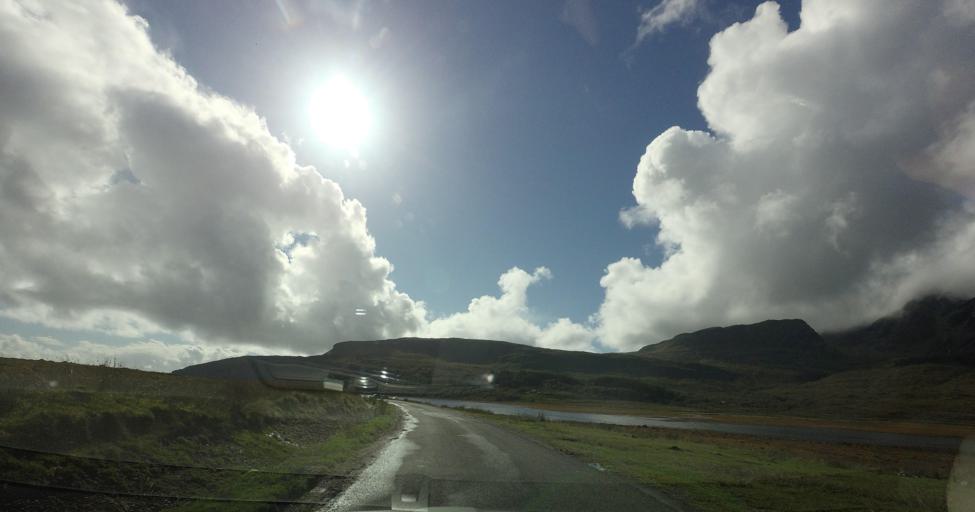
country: GB
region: Scotland
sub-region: Highland
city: Portree
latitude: 57.2233
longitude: -6.0296
